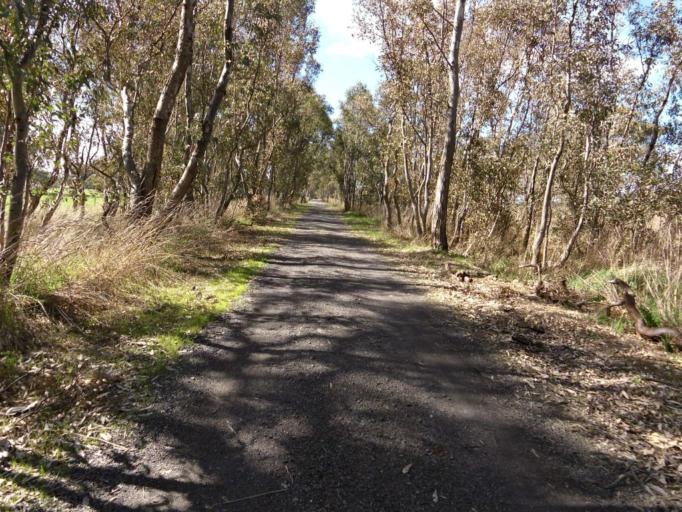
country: AU
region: Victoria
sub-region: Mansfield
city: Mansfield
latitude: -37.0458
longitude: 146.0521
